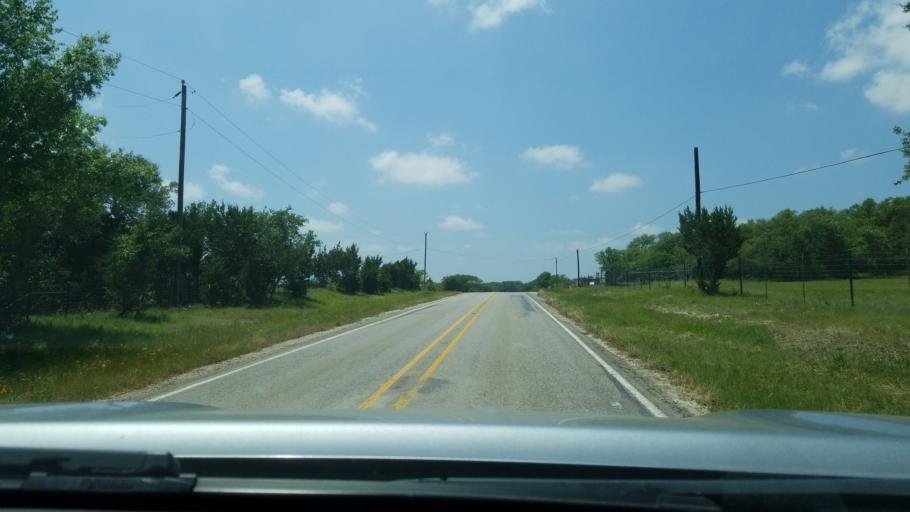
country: US
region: Texas
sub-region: Hays County
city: Woodcreek
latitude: 30.0987
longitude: -98.2503
